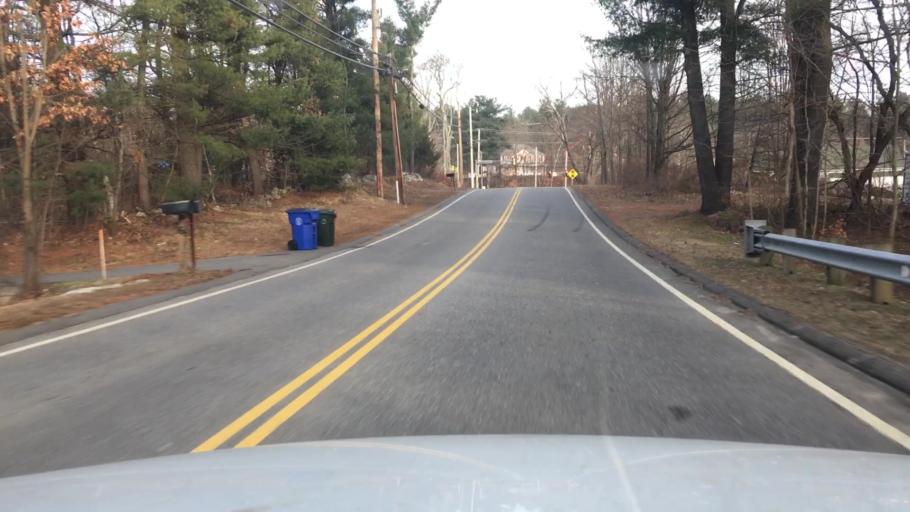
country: US
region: New Hampshire
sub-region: Rockingham County
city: Londonderry
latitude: 42.8978
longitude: -71.3887
